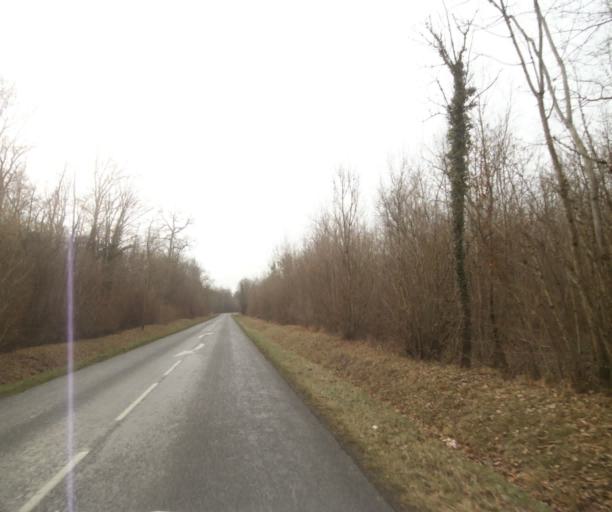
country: FR
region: Champagne-Ardenne
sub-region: Departement de la Haute-Marne
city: Villiers-en-Lieu
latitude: 48.6904
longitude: 4.8894
